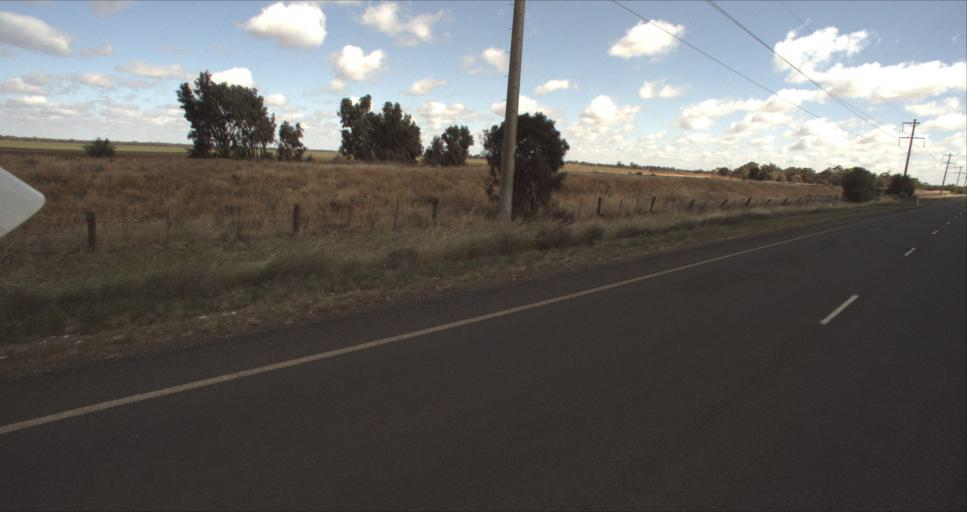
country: AU
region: New South Wales
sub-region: Murrumbidgee Shire
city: Darlington Point
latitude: -34.5356
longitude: 146.1731
